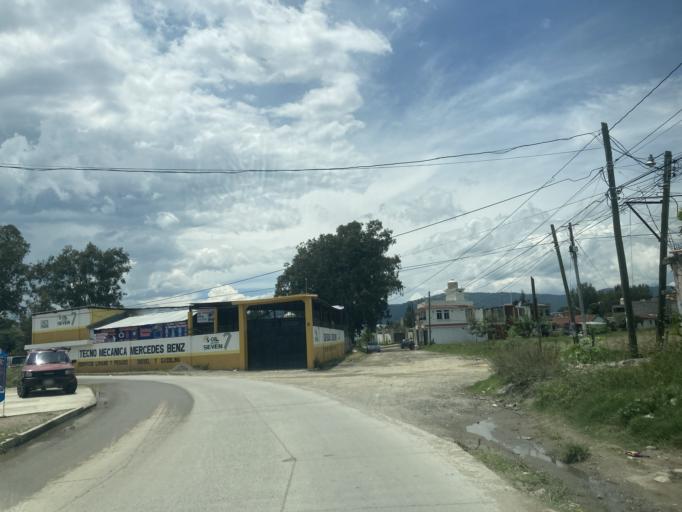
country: GT
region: Huehuetenango
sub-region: Municipio de Huehuetenango
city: Huehuetenango
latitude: 15.3245
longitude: -91.4955
